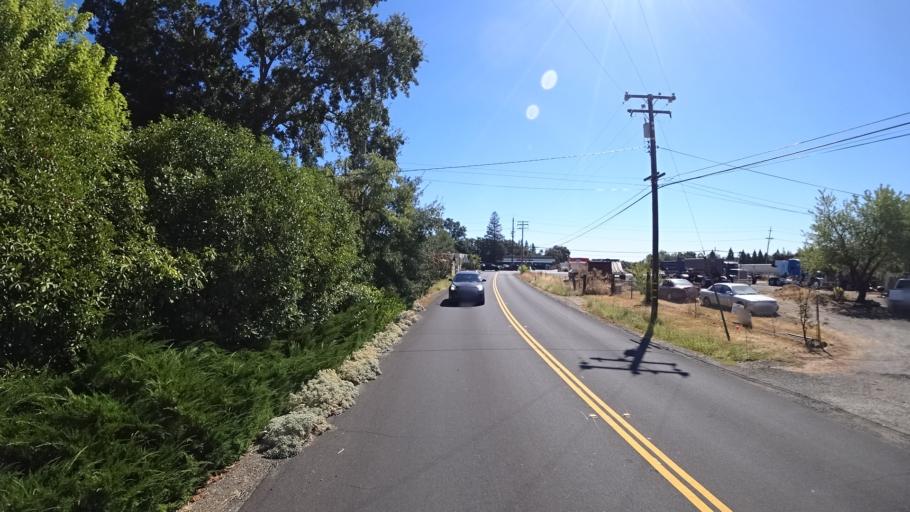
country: US
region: California
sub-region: Sacramento County
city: Wilton
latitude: 38.4309
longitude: -121.3023
